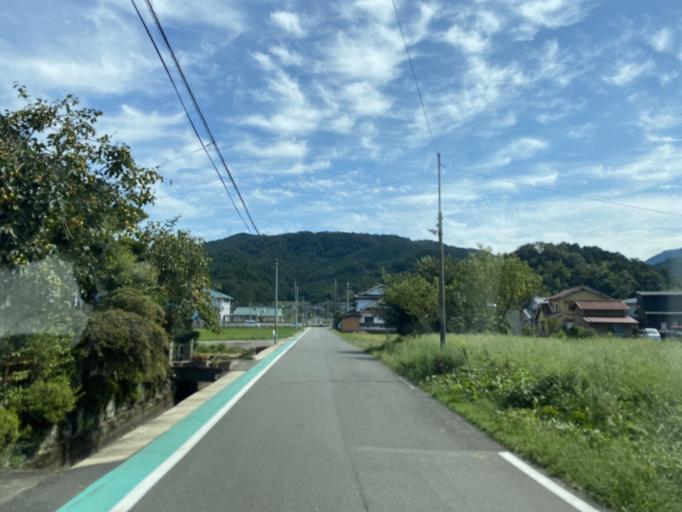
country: JP
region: Hyogo
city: Toyooka
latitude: 35.4311
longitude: 134.7936
